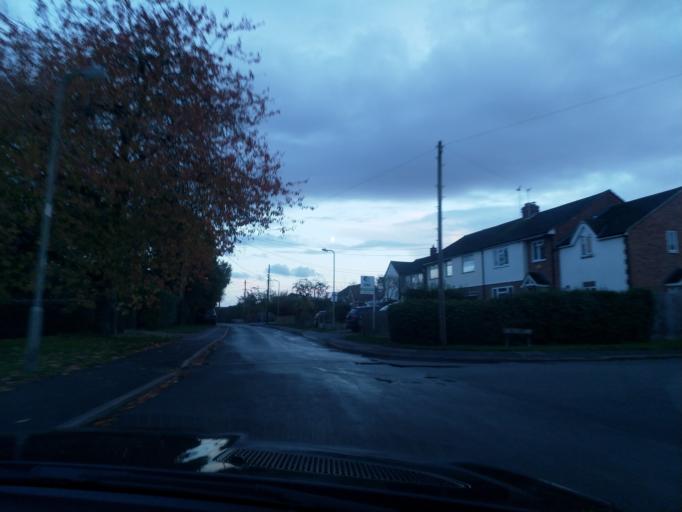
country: GB
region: England
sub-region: Oxfordshire
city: Wheatley
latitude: 51.7448
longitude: -1.1312
